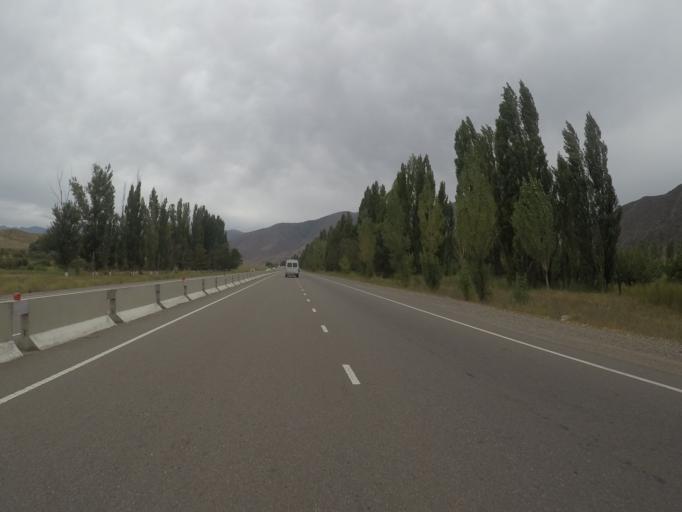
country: KG
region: Chuy
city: Bystrovka
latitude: 42.7349
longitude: 75.8373
